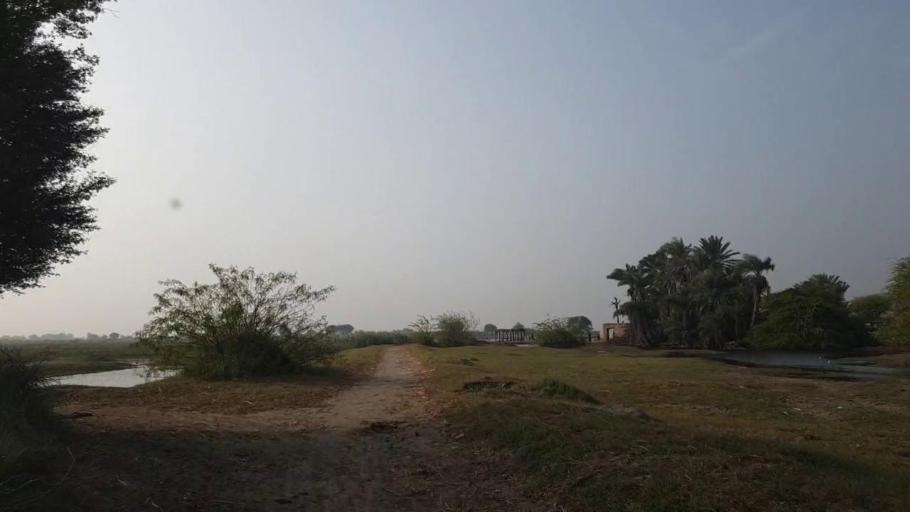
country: PK
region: Sindh
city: Matli
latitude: 25.0647
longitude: 68.6093
